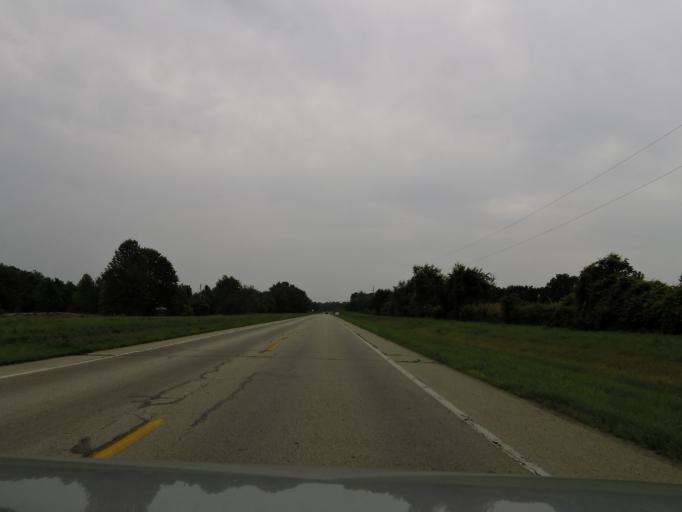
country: US
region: Ohio
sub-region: Brown County
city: Ripley
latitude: 38.8136
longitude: -83.8063
